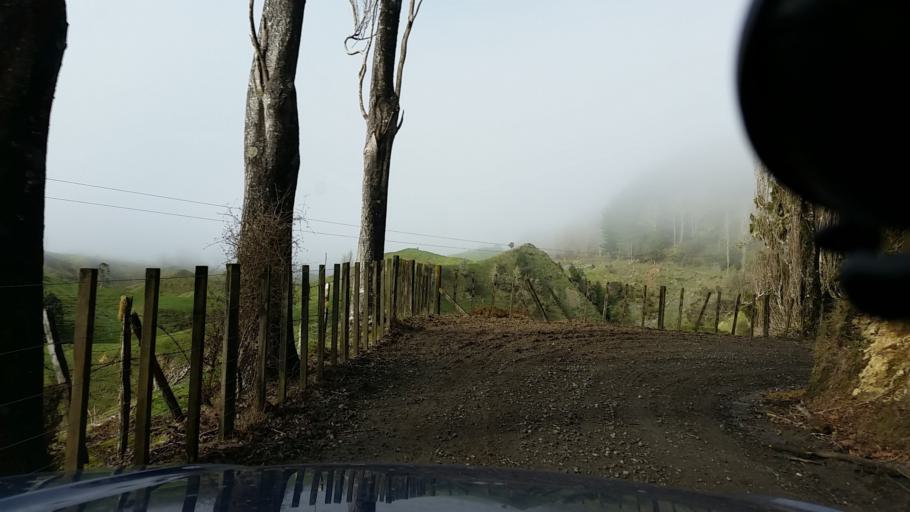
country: NZ
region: Taranaki
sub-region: New Plymouth District
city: Waitara
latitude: -39.0035
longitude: 174.7645
